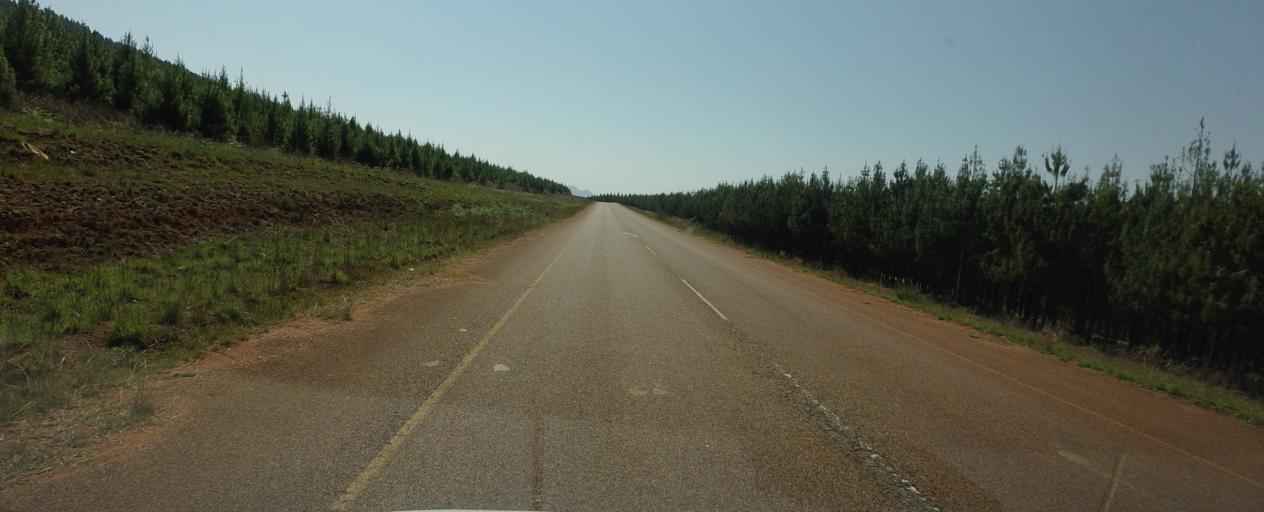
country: ZA
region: Mpumalanga
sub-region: Ehlanzeni District
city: Graksop
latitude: -24.7593
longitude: 30.8579
